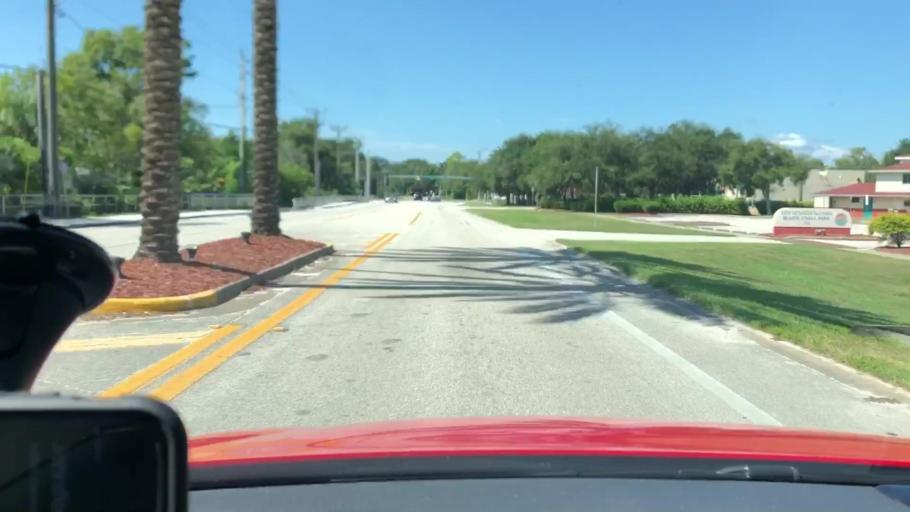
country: US
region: Florida
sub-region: Volusia County
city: South Daytona
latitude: 29.1665
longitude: -81.0213
